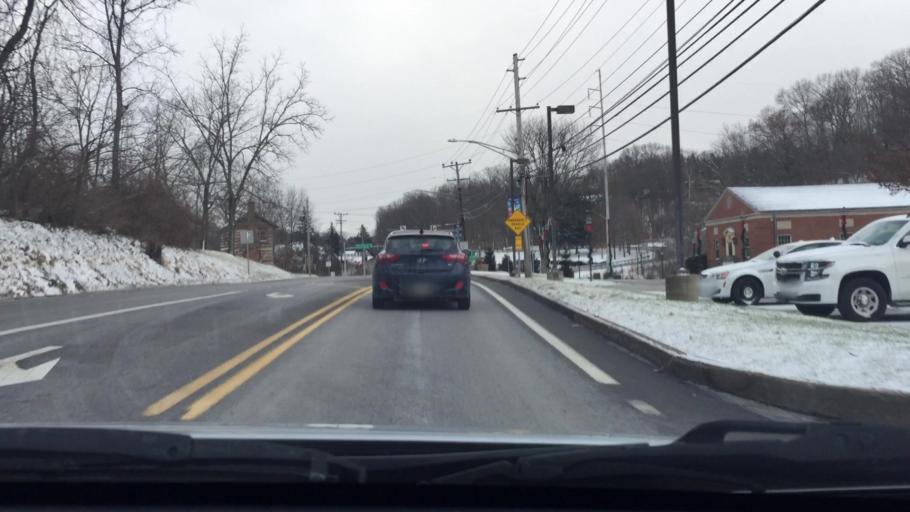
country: US
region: Pennsylvania
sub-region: Allegheny County
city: Upper Saint Clair
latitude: 40.3337
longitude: -80.0714
